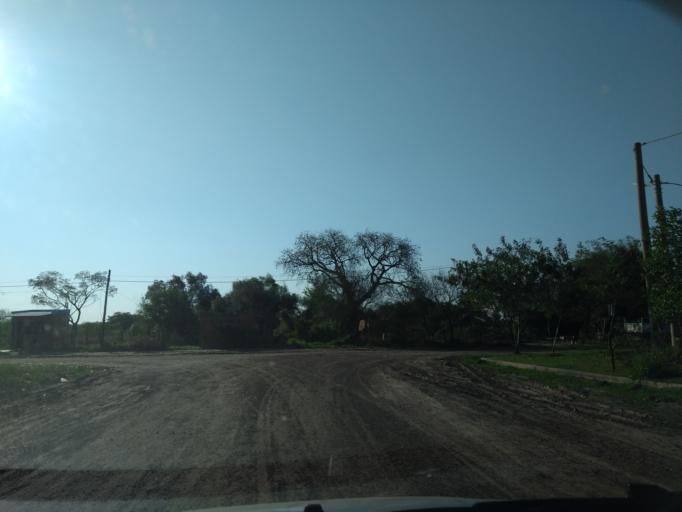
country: AR
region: Chaco
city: Fontana
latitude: -27.4142
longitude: -59.0568
